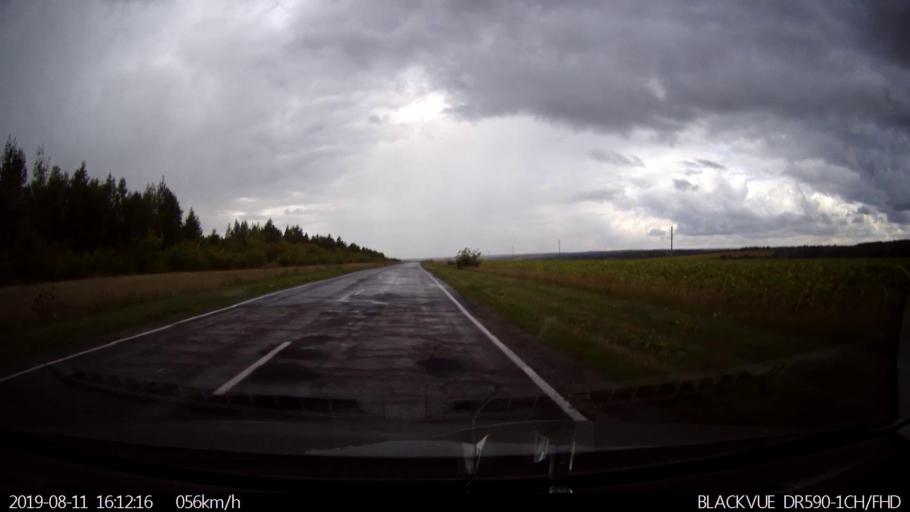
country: RU
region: Ulyanovsk
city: Ignatovka
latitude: 54.0101
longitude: 47.6410
